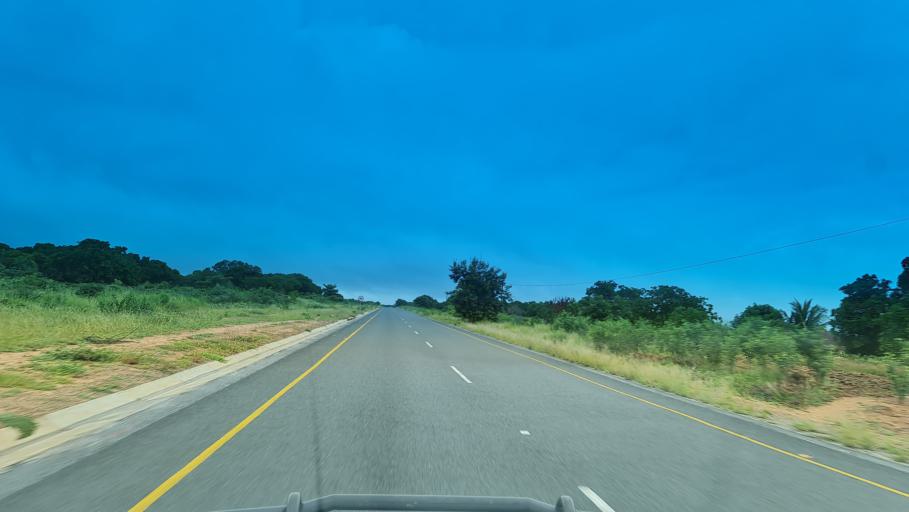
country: MZ
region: Nampula
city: Nampula
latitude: -15.5889
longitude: 39.3250
